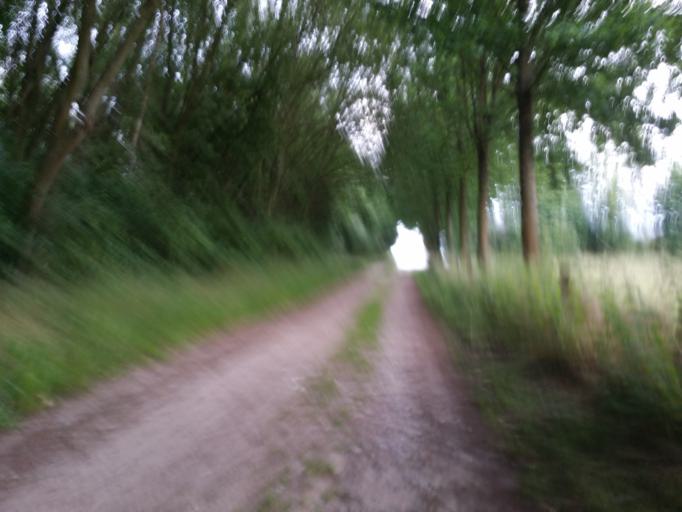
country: DE
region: Lower Saxony
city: Ganderkesee
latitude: 53.0402
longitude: 8.5812
